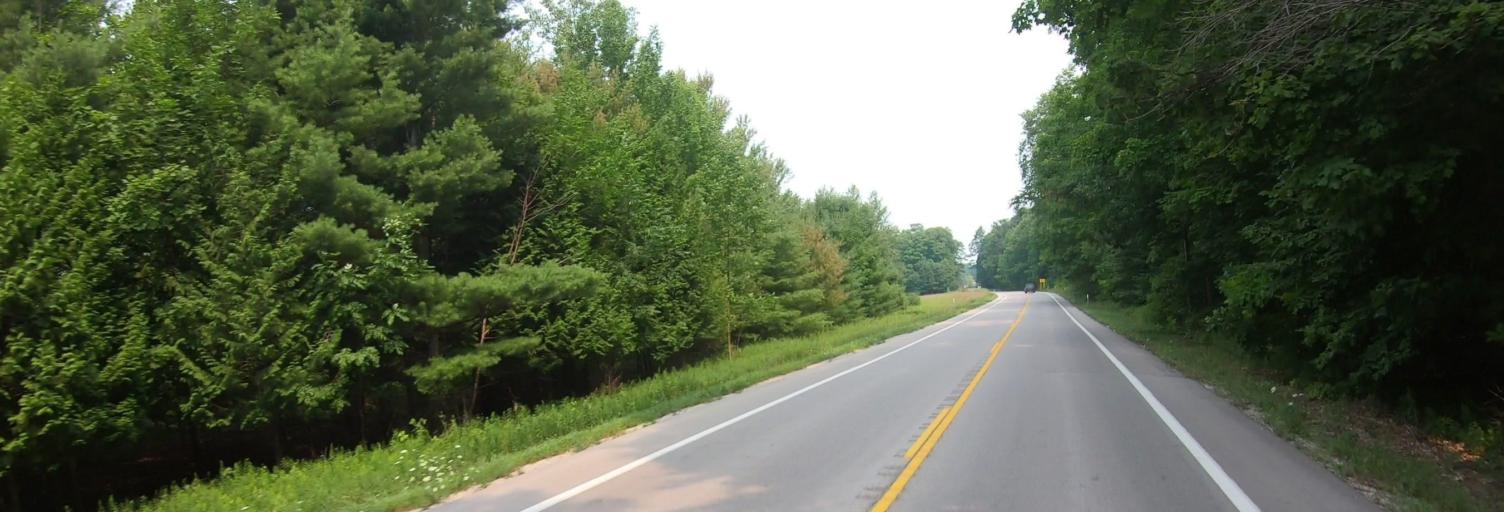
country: US
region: Michigan
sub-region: Leelanau County
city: Leland
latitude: 44.9289
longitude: -85.8172
